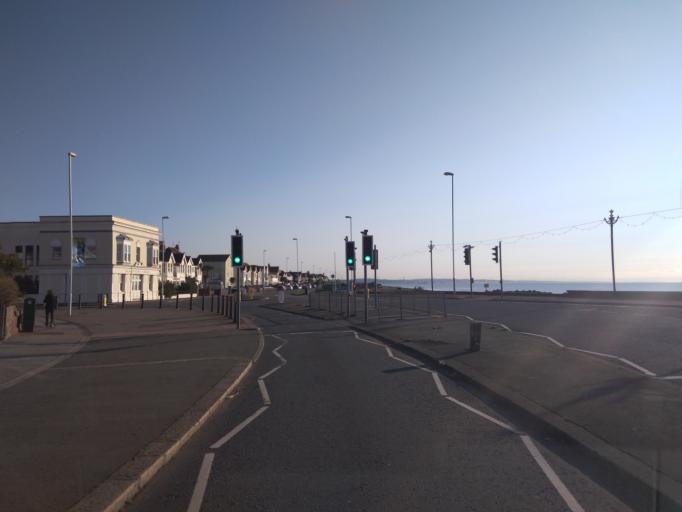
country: GB
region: England
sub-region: West Sussex
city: Worthing
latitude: 50.8131
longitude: -0.3522
